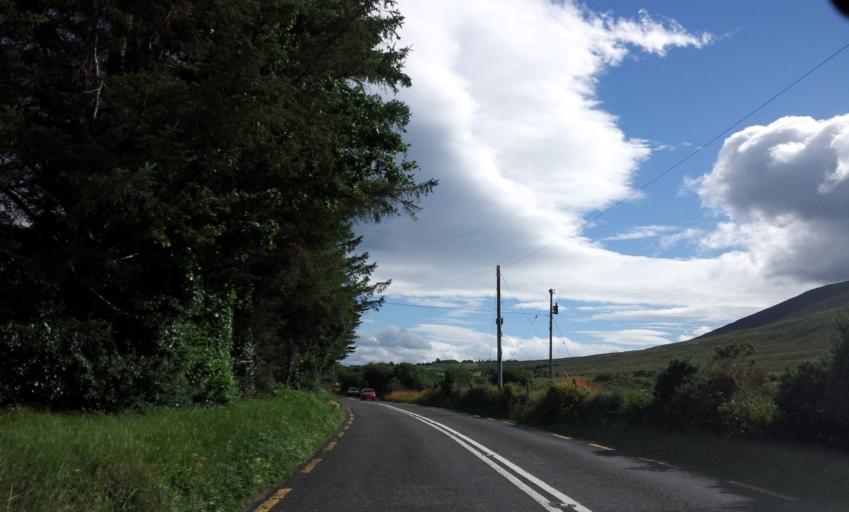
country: IE
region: Munster
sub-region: Ciarrai
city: Killorglin
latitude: 52.2317
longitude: -9.8652
